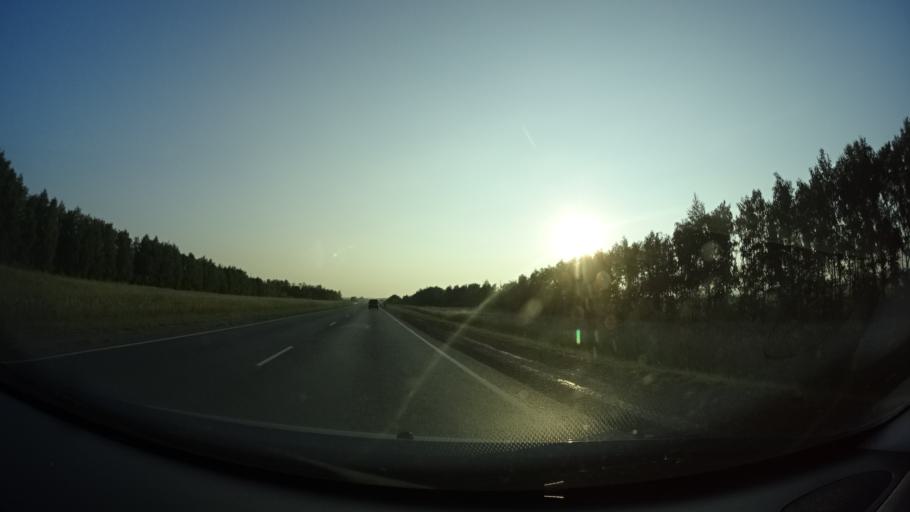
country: RU
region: Samara
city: Klyavlino
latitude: 54.0235
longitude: 51.8573
